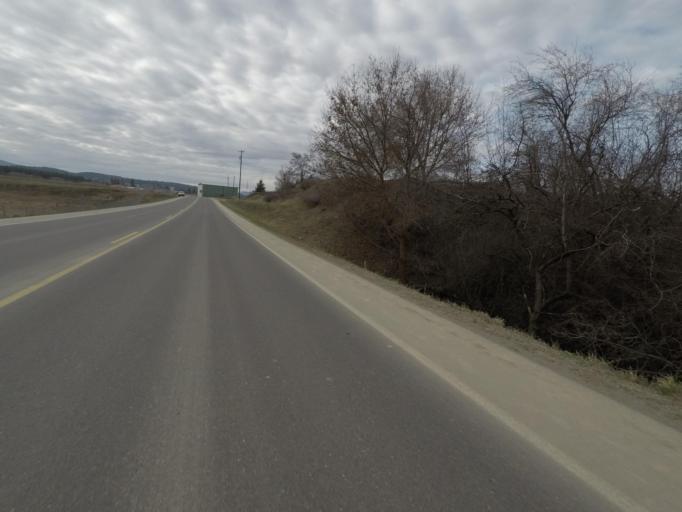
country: US
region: Washington
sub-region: Stevens County
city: Colville
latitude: 48.5489
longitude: -117.8821
